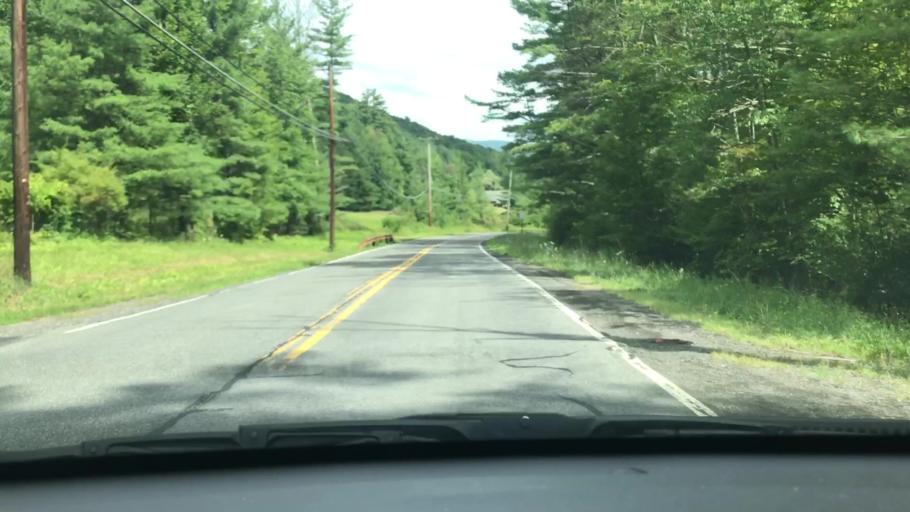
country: US
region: New York
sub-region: Ulster County
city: Shokan
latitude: 41.9969
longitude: -74.2774
